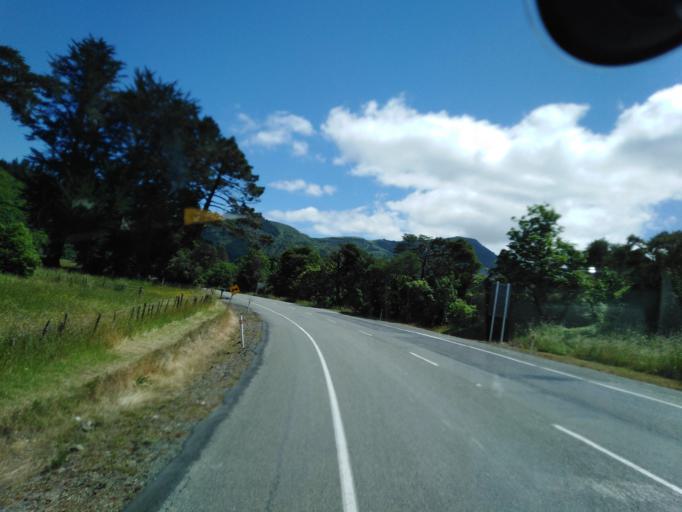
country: NZ
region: Nelson
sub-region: Nelson City
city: Nelson
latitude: -41.2198
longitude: 173.3979
